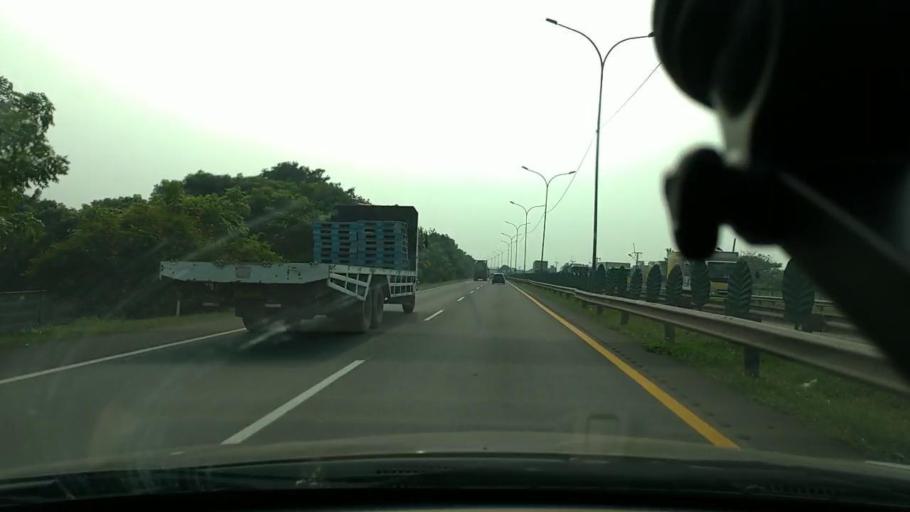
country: ID
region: Banten
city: Serang
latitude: -6.1036
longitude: 106.1747
